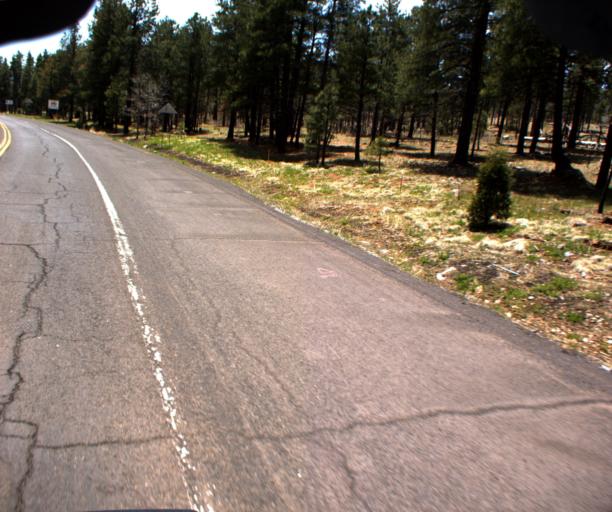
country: US
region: Arizona
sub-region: Coconino County
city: Kachina Village
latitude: 35.0348
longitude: -111.7343
